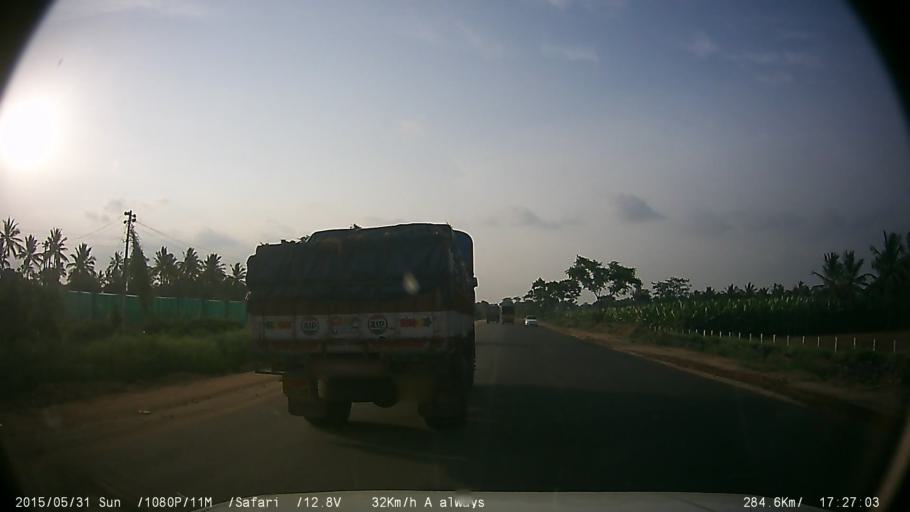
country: IN
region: Karnataka
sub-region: Chamrajnagar
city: Gundlupet
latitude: 11.8573
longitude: 76.6703
